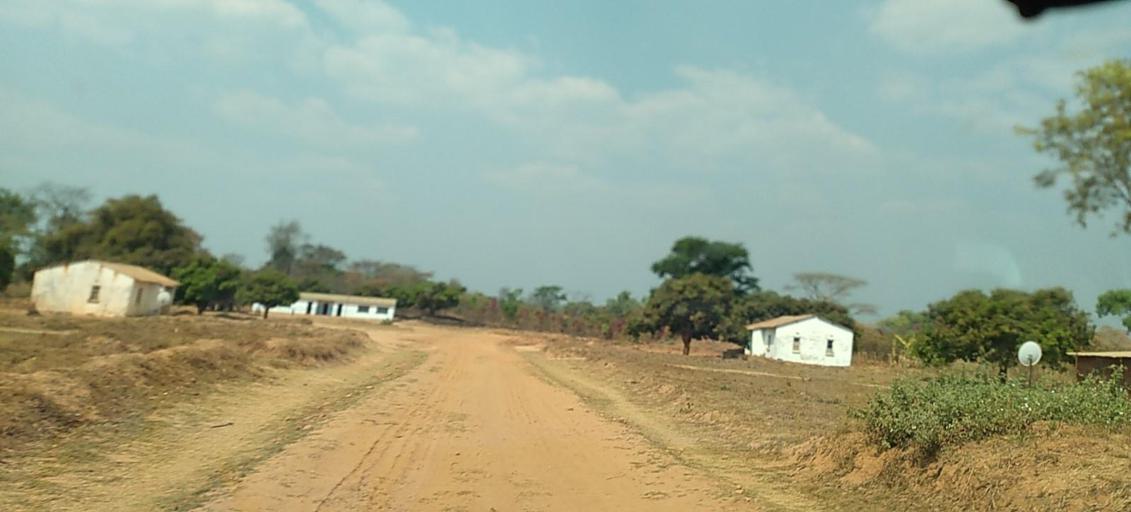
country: ZM
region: North-Western
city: Kasempa
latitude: -13.3048
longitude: 26.0768
